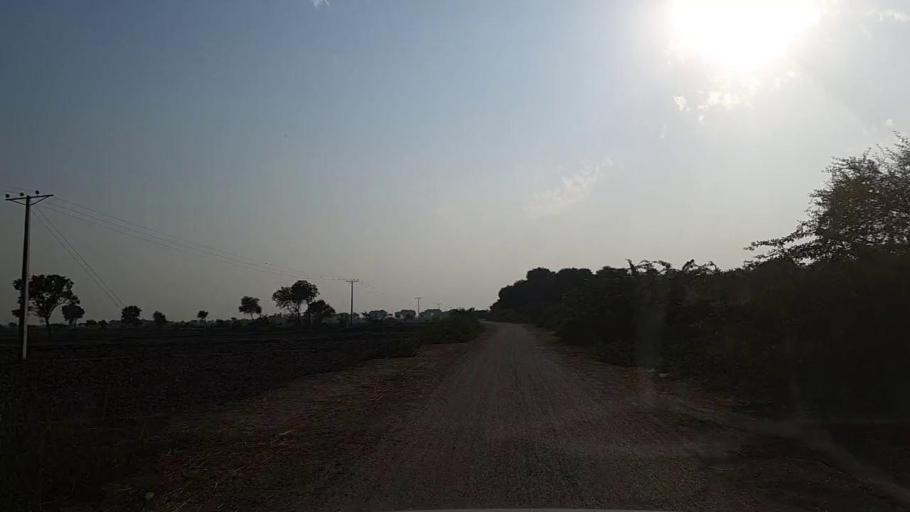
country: PK
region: Sindh
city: Mirpur Batoro
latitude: 24.7831
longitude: 68.2452
